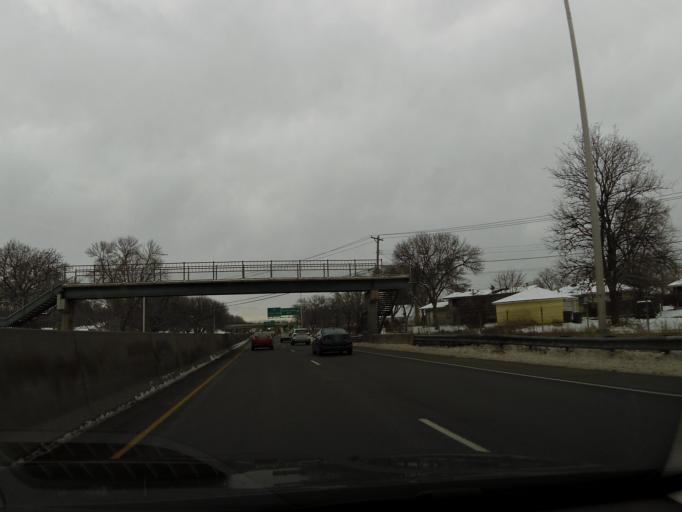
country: US
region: Minnesota
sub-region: Hennepin County
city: Richfield
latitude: 44.8914
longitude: -93.2554
